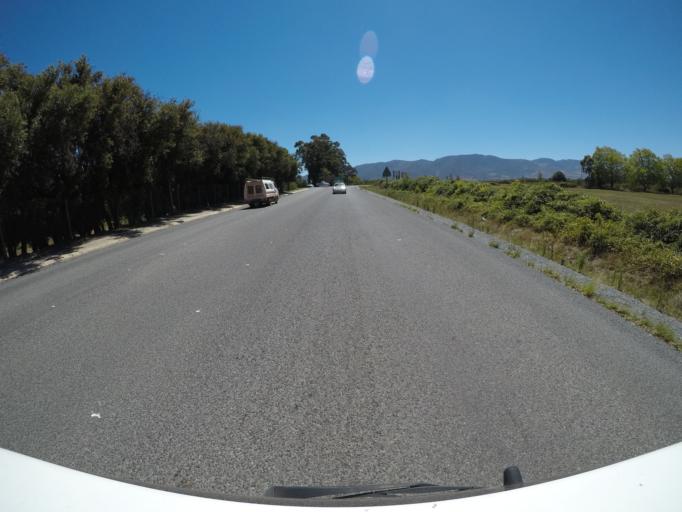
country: ZA
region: Western Cape
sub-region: Overberg District Municipality
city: Grabouw
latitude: -34.1659
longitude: 19.0367
